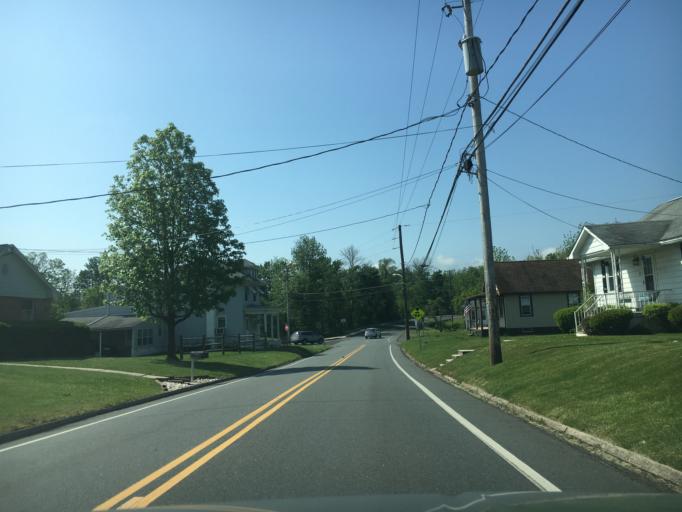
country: US
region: Pennsylvania
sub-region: Berks County
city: Boyertown
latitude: 40.3331
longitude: -75.6233
